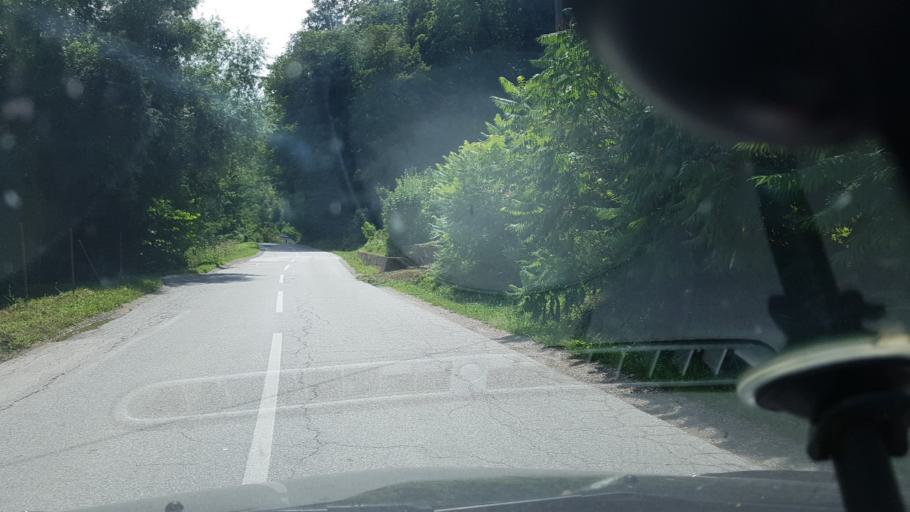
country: HR
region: Krapinsko-Zagorska
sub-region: Grad Krapina
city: Krapina
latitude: 46.1960
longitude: 15.8664
